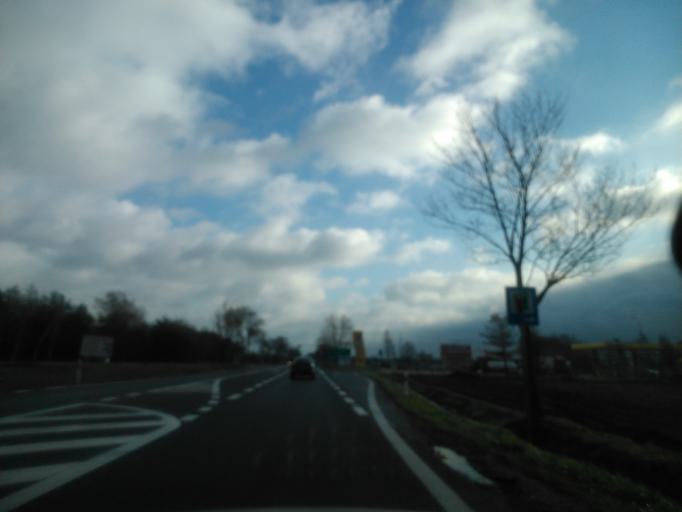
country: PL
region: Masovian Voivodeship
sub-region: Powiat sierpecki
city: Zawidz
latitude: 52.7992
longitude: 19.8591
